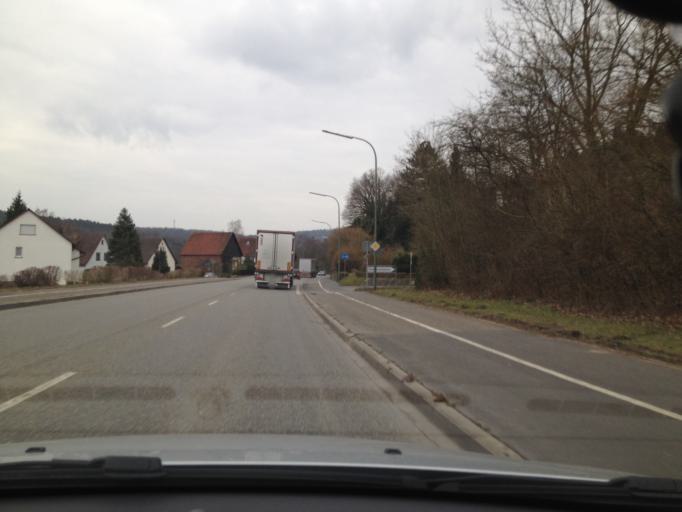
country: DE
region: Bavaria
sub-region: Regierungsbezirk Unterfranken
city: Kreuzwertheim
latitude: 49.7796
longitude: 9.5071
